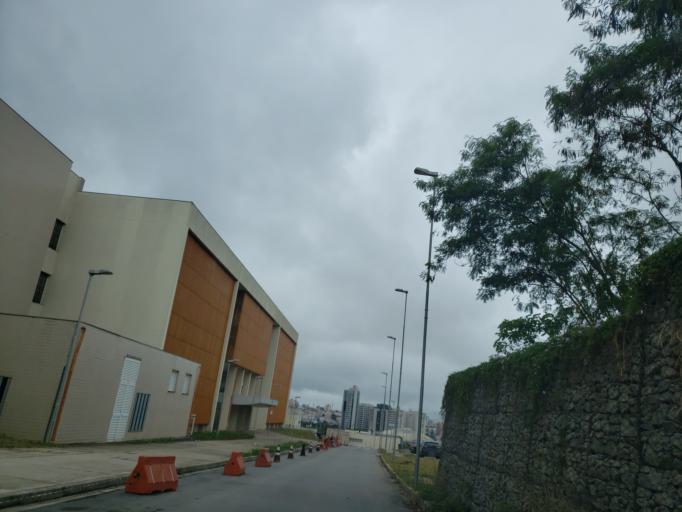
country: BR
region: Sao Paulo
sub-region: Sao Bernardo Do Campo
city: Sao Bernardo do Campo
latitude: -23.6780
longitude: -46.5655
